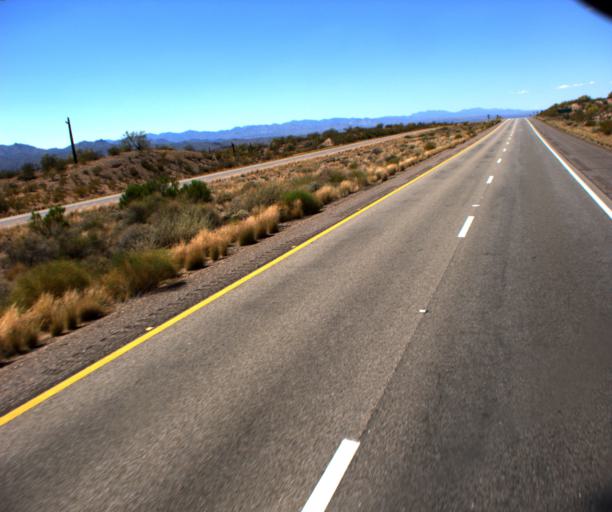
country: US
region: Arizona
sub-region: Yavapai County
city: Bagdad
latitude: 34.6061
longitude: -113.5221
